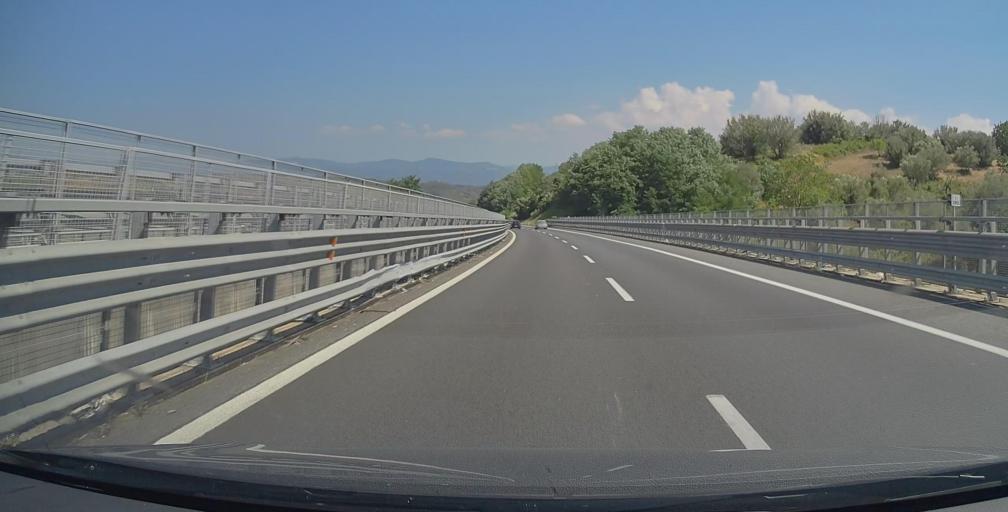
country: IT
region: Calabria
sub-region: Provincia di Vibo-Valentia
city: Sant'Onofrio
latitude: 38.6842
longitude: 16.1644
